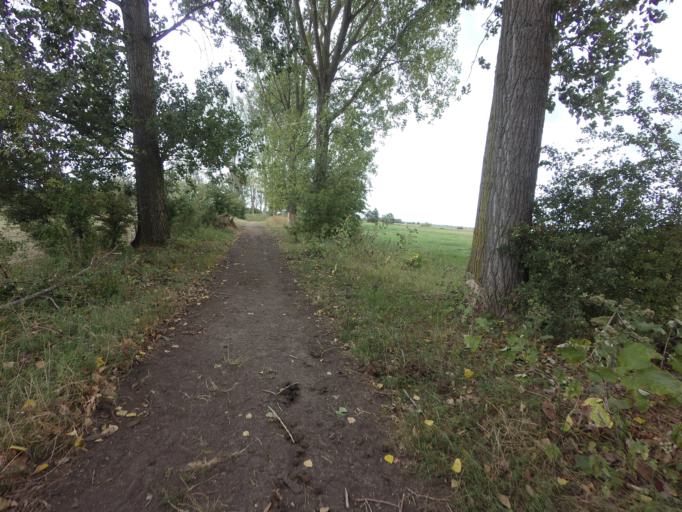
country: NL
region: Limburg
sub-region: Gemeente Maasgouw
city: Maasbracht
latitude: 51.1430
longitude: 5.8633
